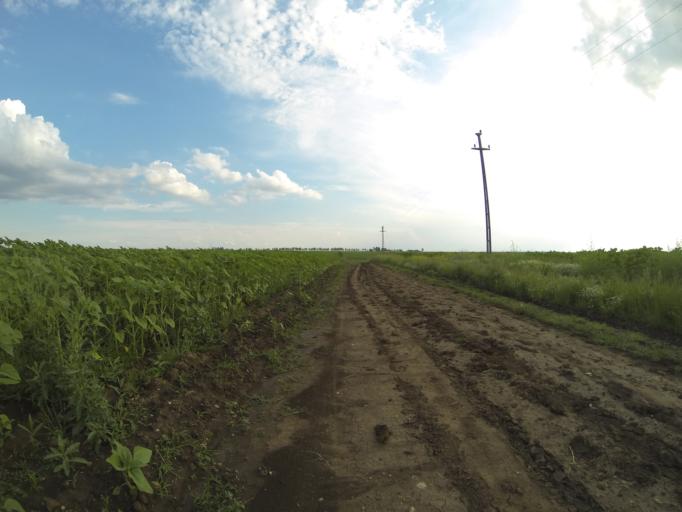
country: RO
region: Dolj
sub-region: Comuna Caloparu
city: Salcuta
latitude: 44.1504
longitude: 23.7027
